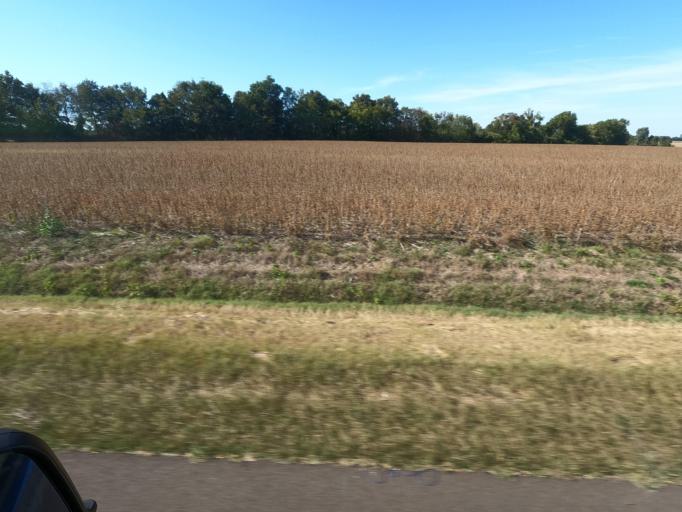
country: US
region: Tennessee
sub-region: Obion County
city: Union City
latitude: 36.3906
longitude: -89.1016
